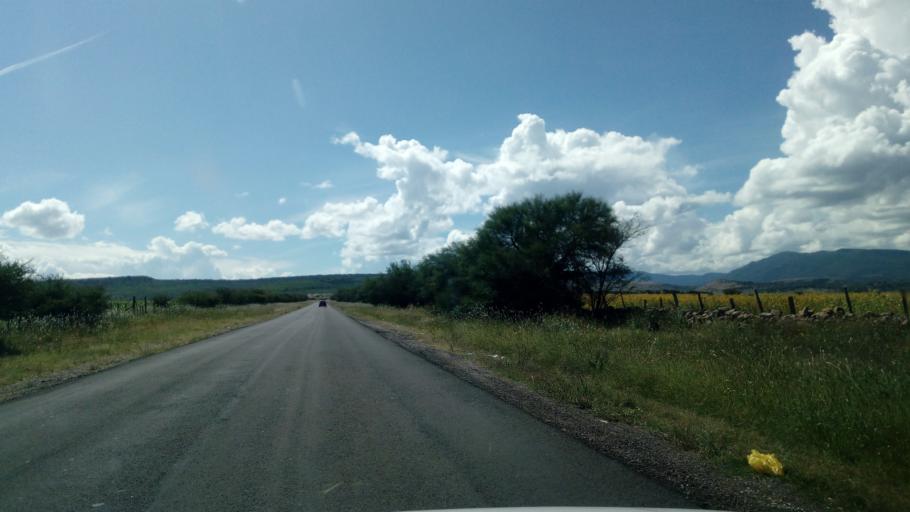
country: MX
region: Durango
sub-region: Durango
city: Jose Refugio Salcido
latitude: 23.8602
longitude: -104.4742
